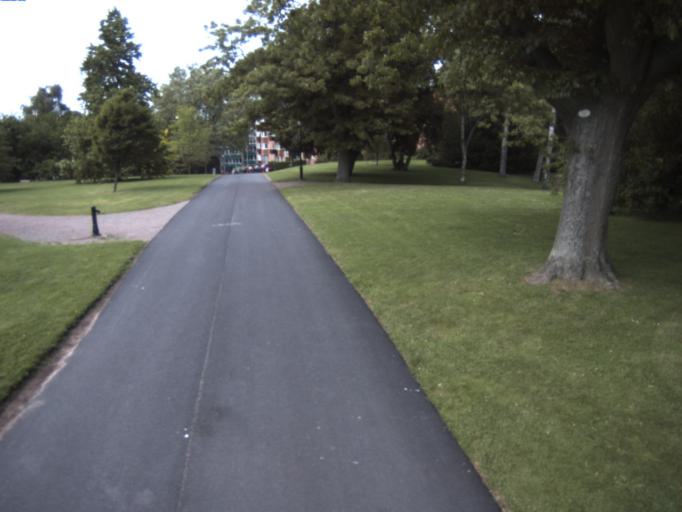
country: SE
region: Skane
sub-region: Helsingborg
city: Helsingborg
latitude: 56.0484
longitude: 12.6981
